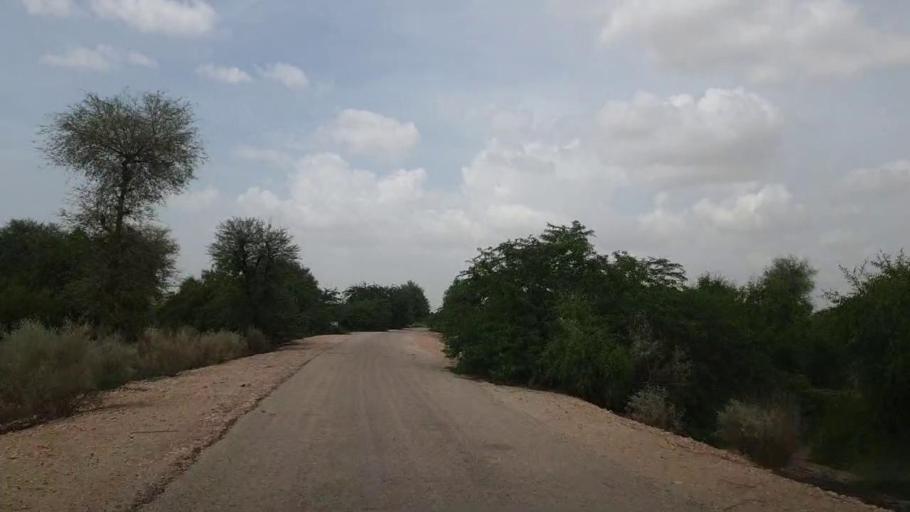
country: PK
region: Sindh
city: Kot Diji
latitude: 27.2203
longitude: 69.0841
